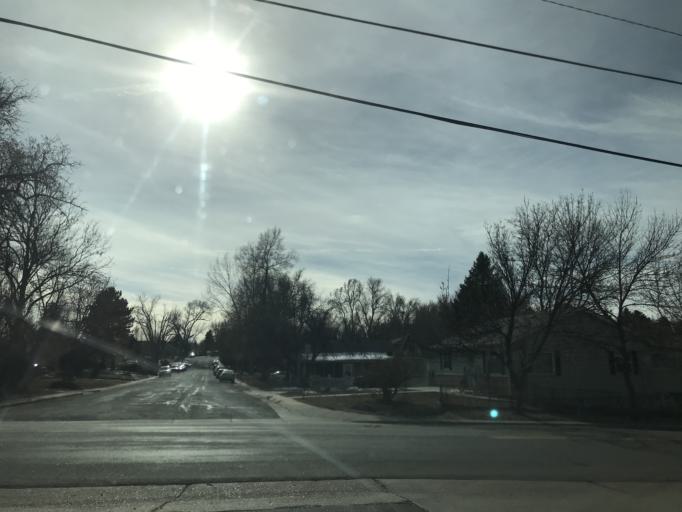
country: US
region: Colorado
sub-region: Arapahoe County
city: Littleton
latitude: 39.6080
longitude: -105.0151
